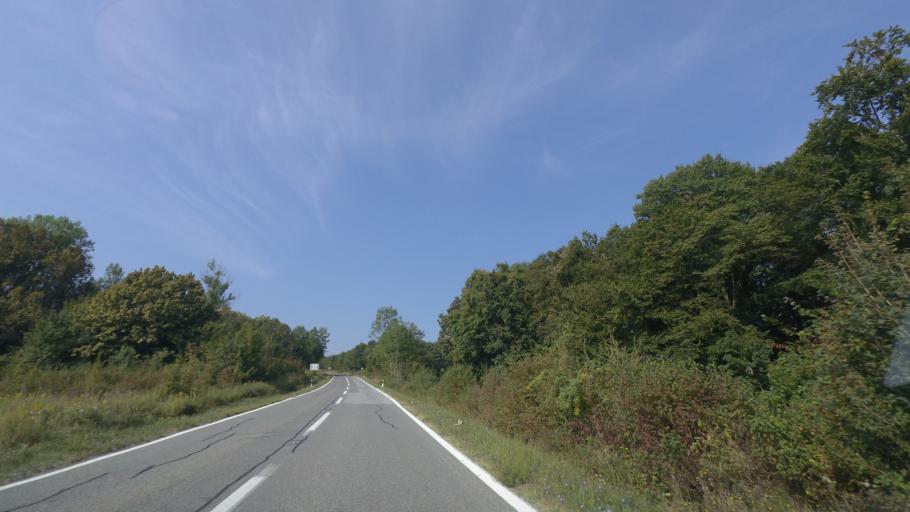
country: HR
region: Pozesko-Slavonska
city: Lipik
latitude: 45.4192
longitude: 17.0856
